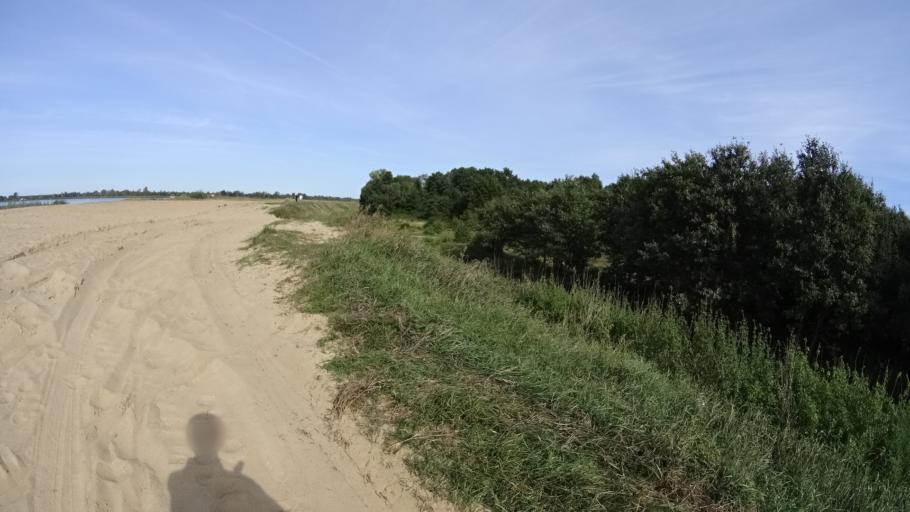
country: PL
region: Masovian Voivodeship
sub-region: Powiat legionowski
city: Serock
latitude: 52.5023
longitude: 21.0850
